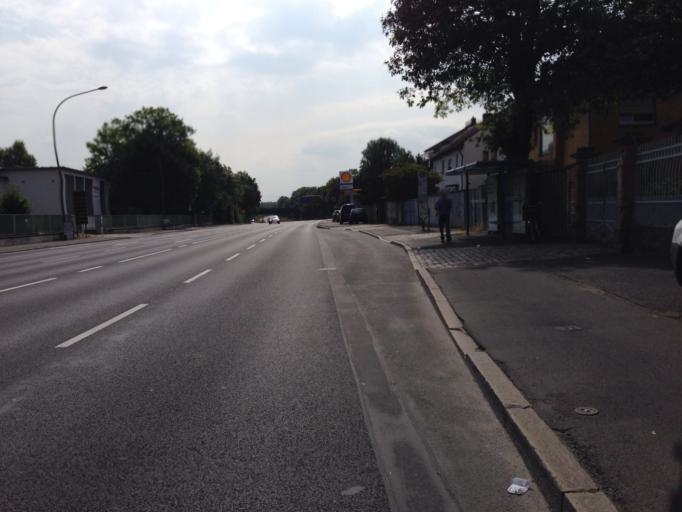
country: DE
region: Hesse
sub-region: Regierungsbezirk Darmstadt
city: Hanau am Main
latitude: 50.1283
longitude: 8.9339
